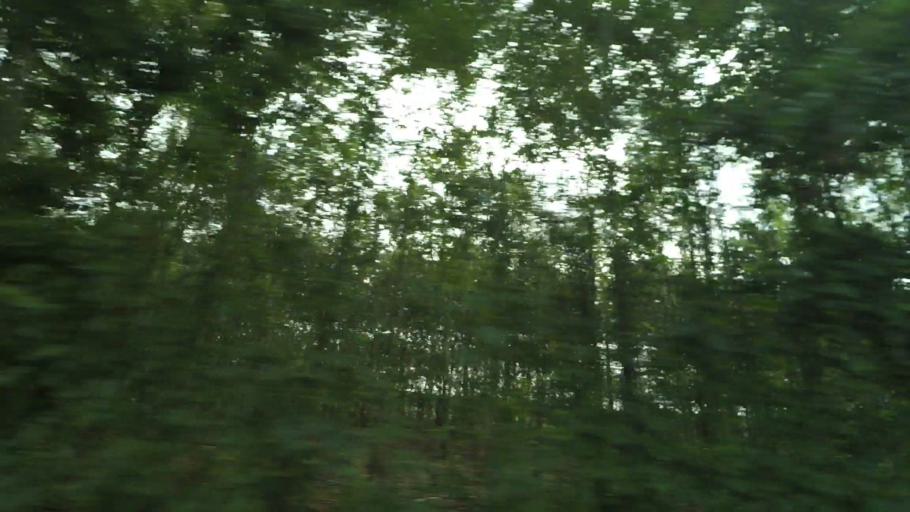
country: DK
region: Central Jutland
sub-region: Syddjurs Kommune
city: Ryomgard
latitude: 56.4401
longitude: 10.5599
